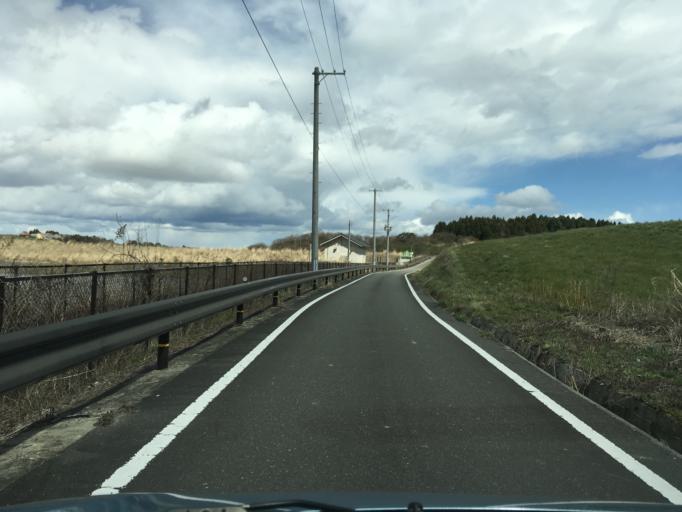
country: JP
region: Miyagi
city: Kogota
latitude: 38.6863
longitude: 141.0985
